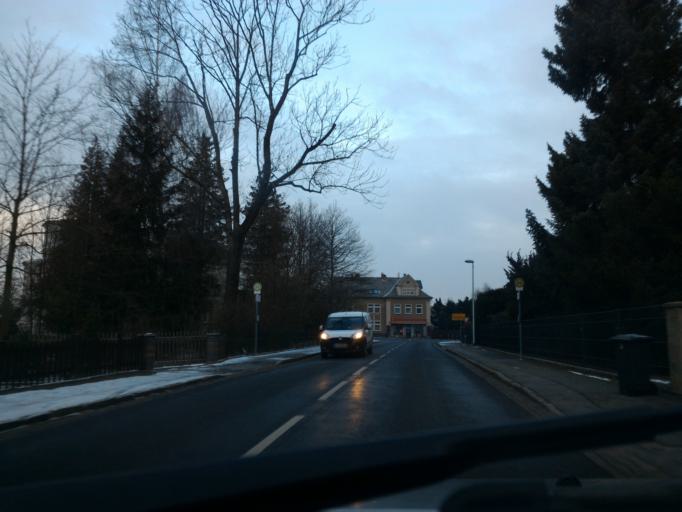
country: DE
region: Saxony
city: Leutersdorf
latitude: 50.9547
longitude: 14.6535
